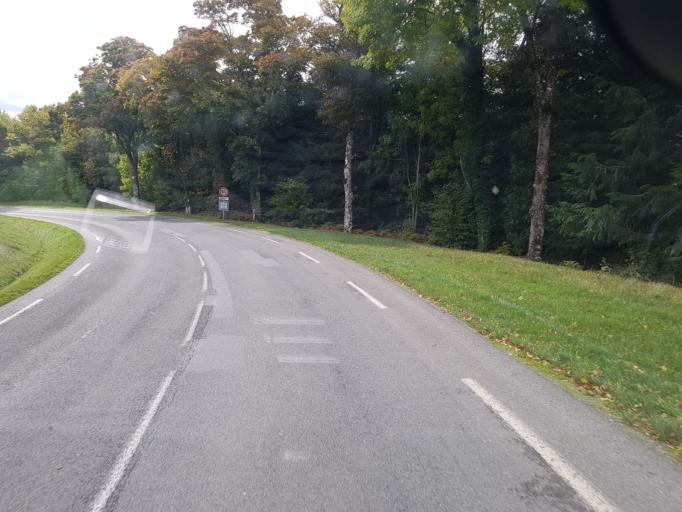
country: FR
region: Languedoc-Roussillon
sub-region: Departement de l'Aude
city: Cuxac-Cabardes
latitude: 43.4130
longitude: 2.2978
